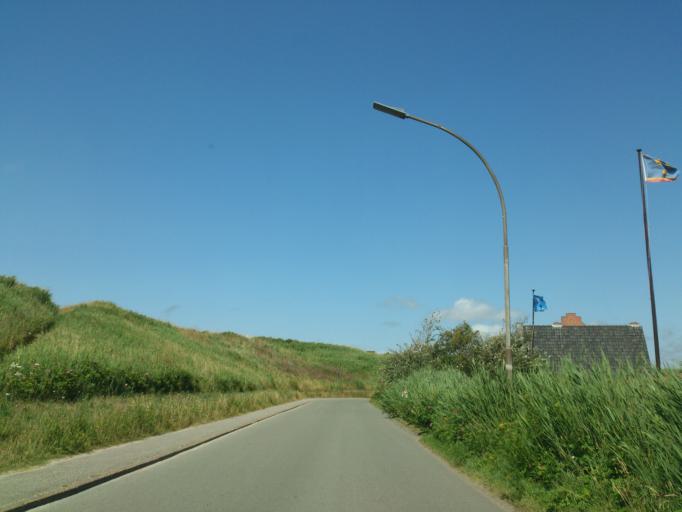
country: DE
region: Schleswig-Holstein
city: Sankt Peter-Ording
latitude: 54.3395
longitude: 8.6023
